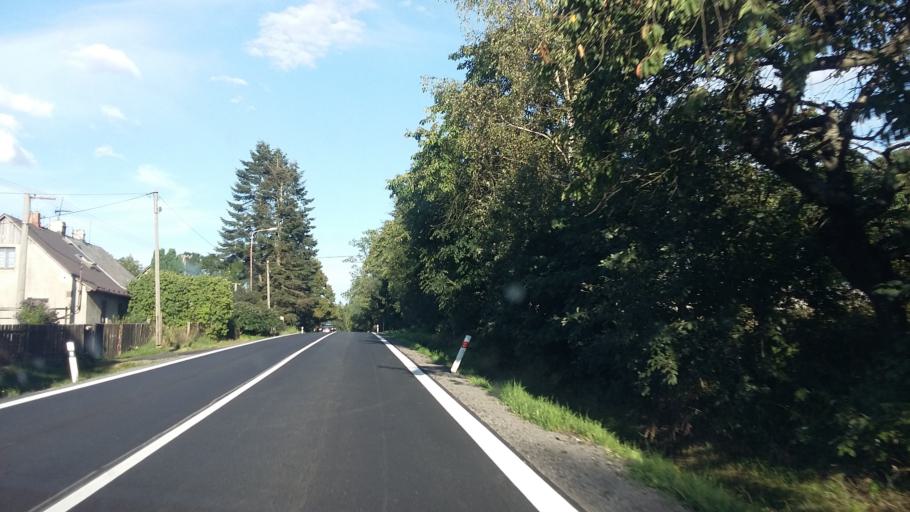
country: CZ
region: Central Bohemia
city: Rozmital pod Tremsinem
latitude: 49.6226
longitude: 13.7542
